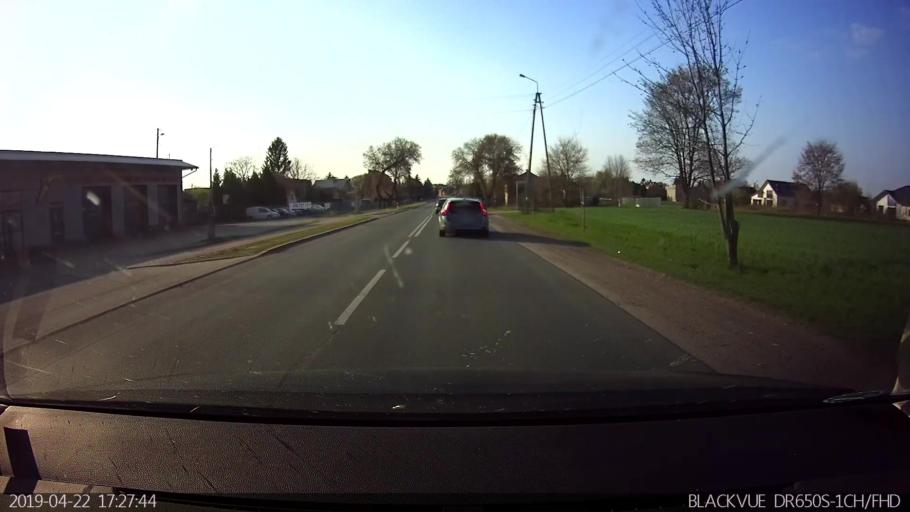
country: PL
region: Masovian Voivodeship
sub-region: Powiat sokolowski
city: Sokolow Podlaski
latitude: 52.3987
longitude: 22.2630
